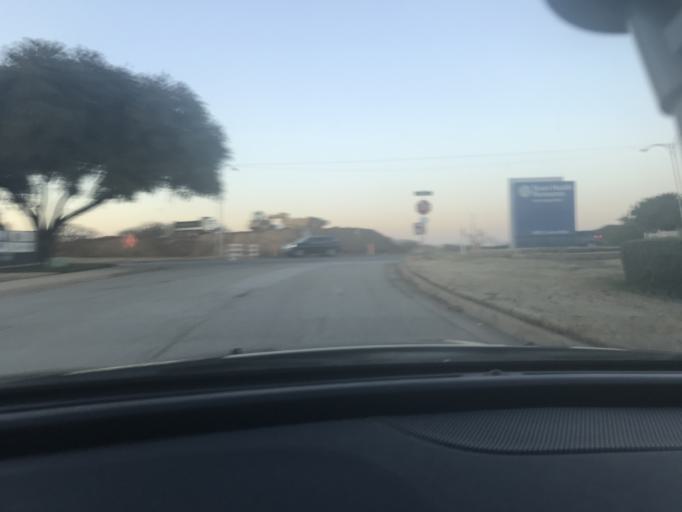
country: US
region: Texas
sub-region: Tarrant County
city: Arlington
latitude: 32.7621
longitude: -97.1056
